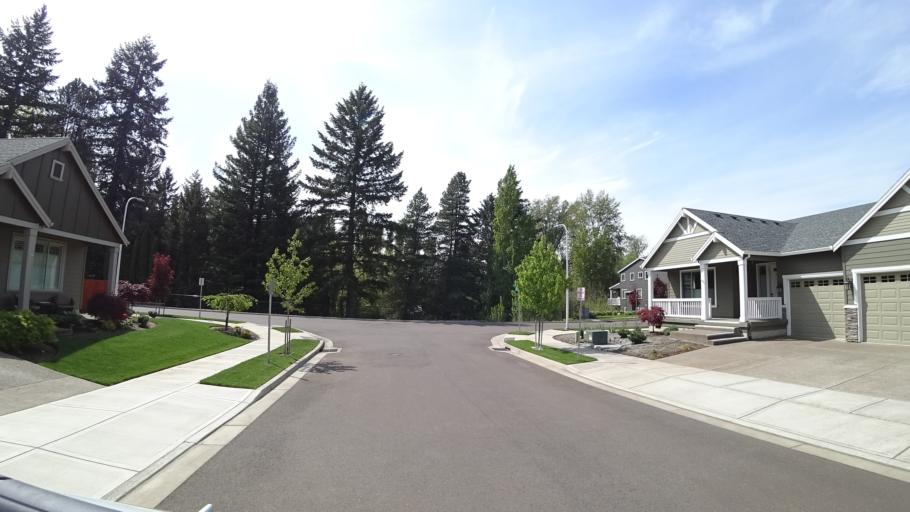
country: US
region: Oregon
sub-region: Washington County
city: Hillsboro
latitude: 45.5278
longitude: -122.9345
